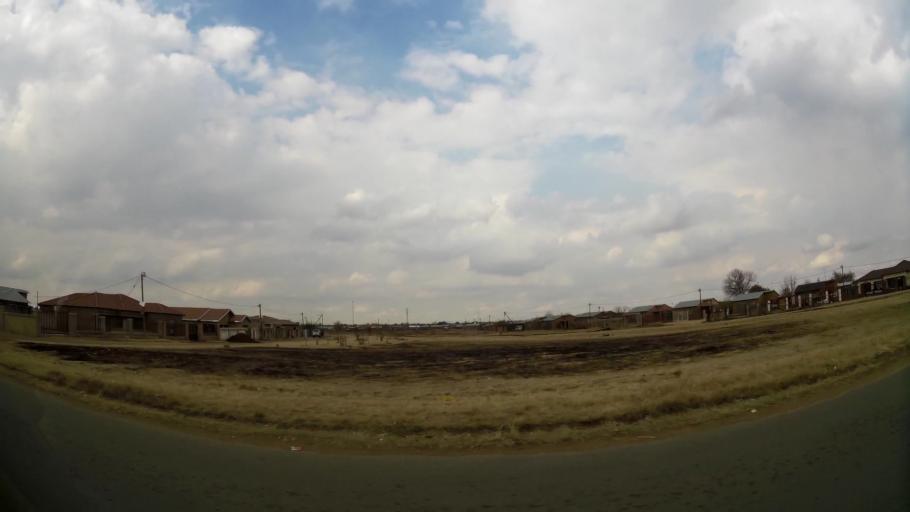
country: ZA
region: Orange Free State
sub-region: Fezile Dabi District Municipality
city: Sasolburg
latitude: -26.8516
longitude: 27.8775
